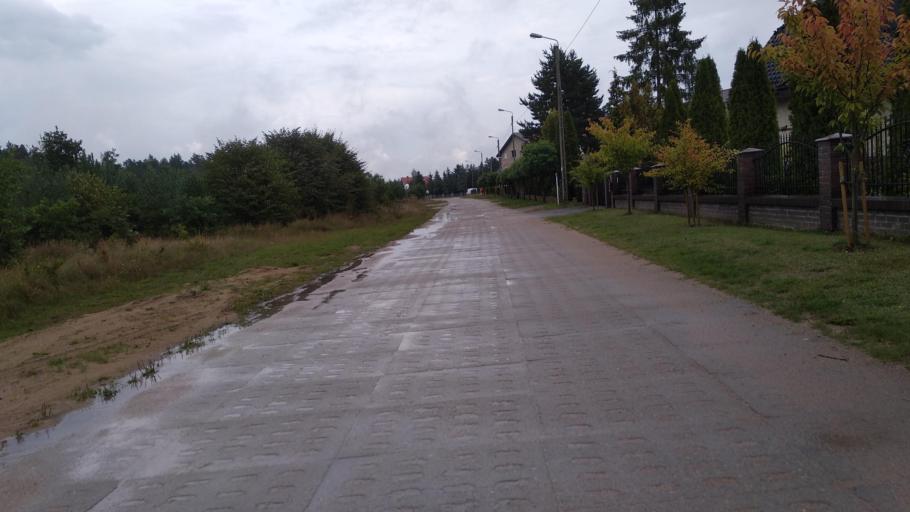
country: PL
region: Pomeranian Voivodeship
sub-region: Powiat wejherowski
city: Bolszewo
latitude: 54.6196
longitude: 18.1625
